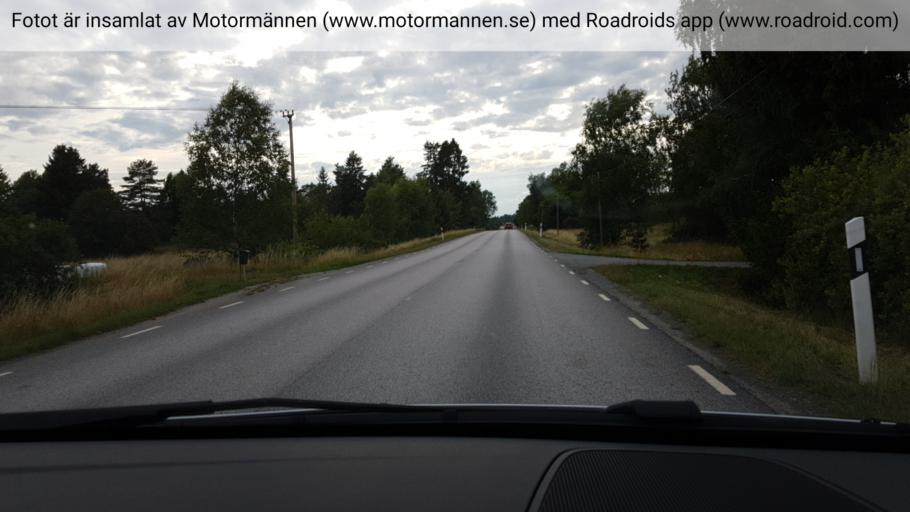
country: SE
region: Stockholm
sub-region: Norrtalje Kommun
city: Skanninge
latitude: 59.9016
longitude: 18.5325
